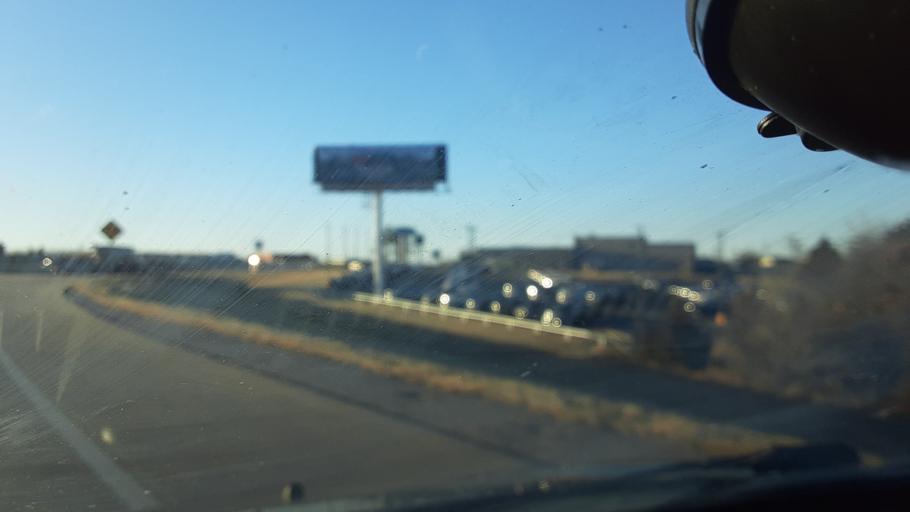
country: US
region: Oklahoma
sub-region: Logan County
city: Guthrie
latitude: 35.8217
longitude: -97.4161
